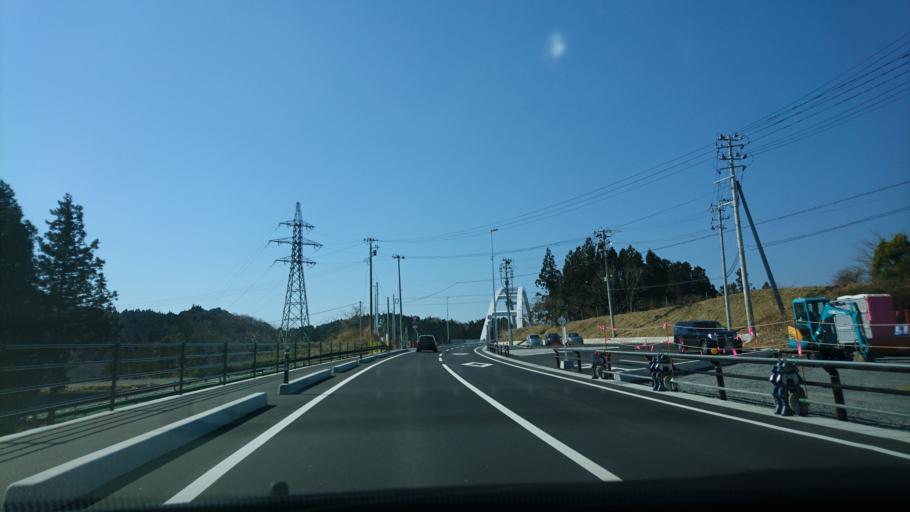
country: JP
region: Iwate
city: Ofunato
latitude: 38.8814
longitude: 141.6072
